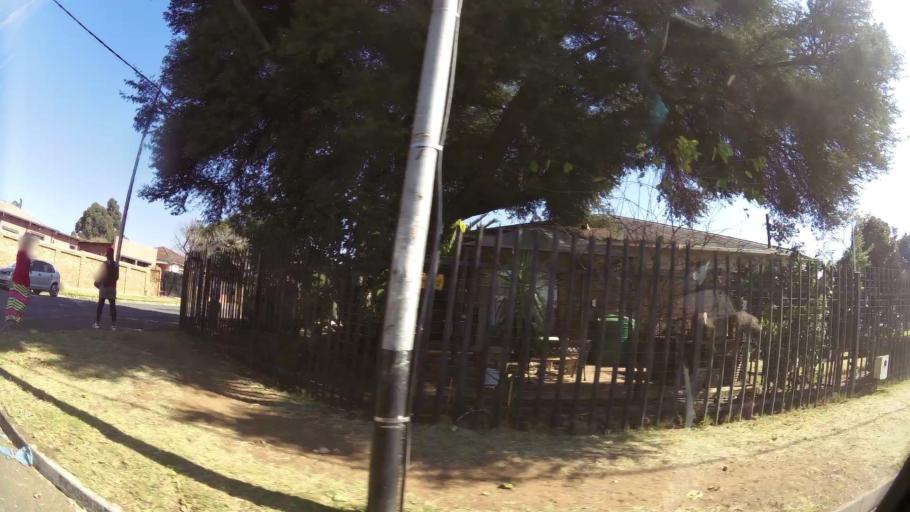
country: ZA
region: Gauteng
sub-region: City of Johannesburg Metropolitan Municipality
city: Johannesburg
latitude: -26.2480
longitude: 28.0918
